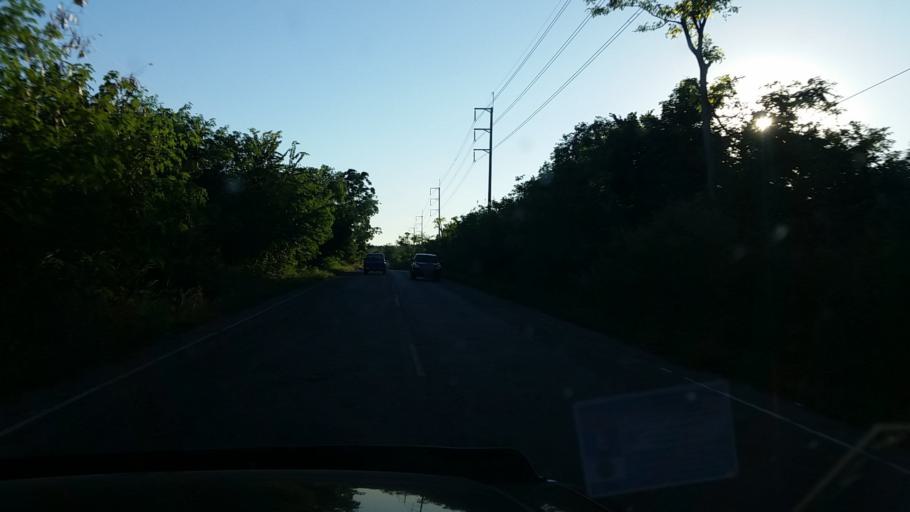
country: TH
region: Chaiyaphum
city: Nong Bua Rawe
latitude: 15.6899
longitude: 101.7059
